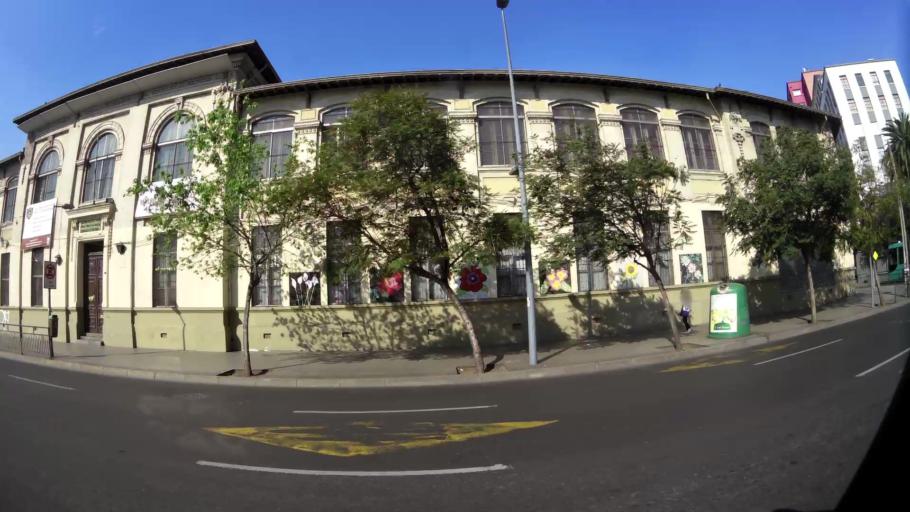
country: CL
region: Santiago Metropolitan
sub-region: Provincia de Santiago
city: Santiago
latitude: -33.4413
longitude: -70.6799
